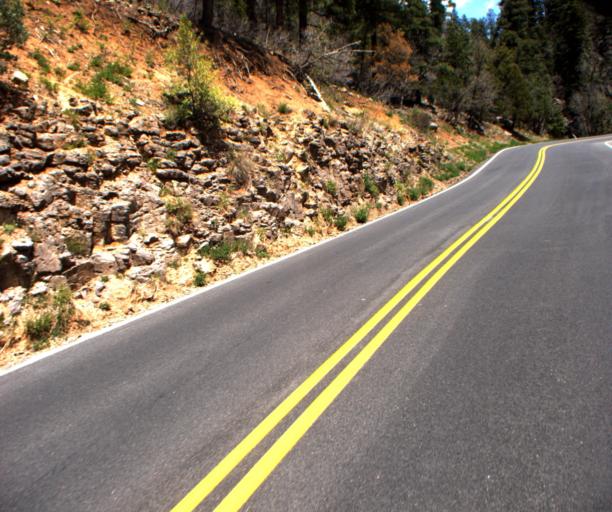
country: US
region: Arizona
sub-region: Coconino County
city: Kachina Village
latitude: 35.0294
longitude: -111.7415
